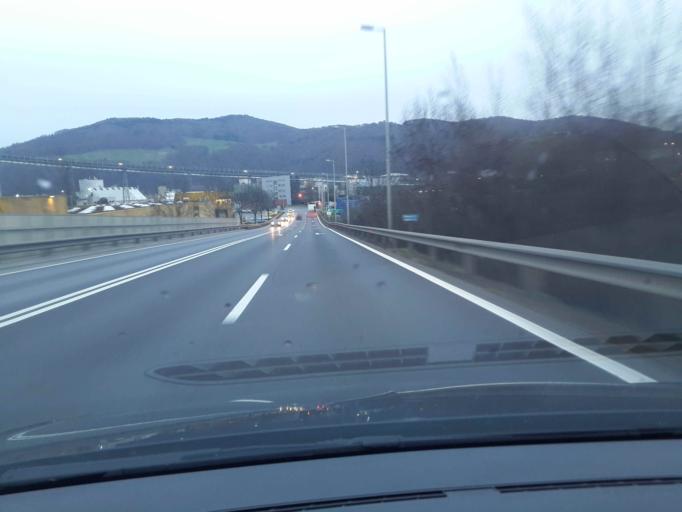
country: AT
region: Upper Austria
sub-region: Linz Stadt
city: Linz
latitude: 48.2966
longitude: 14.3204
